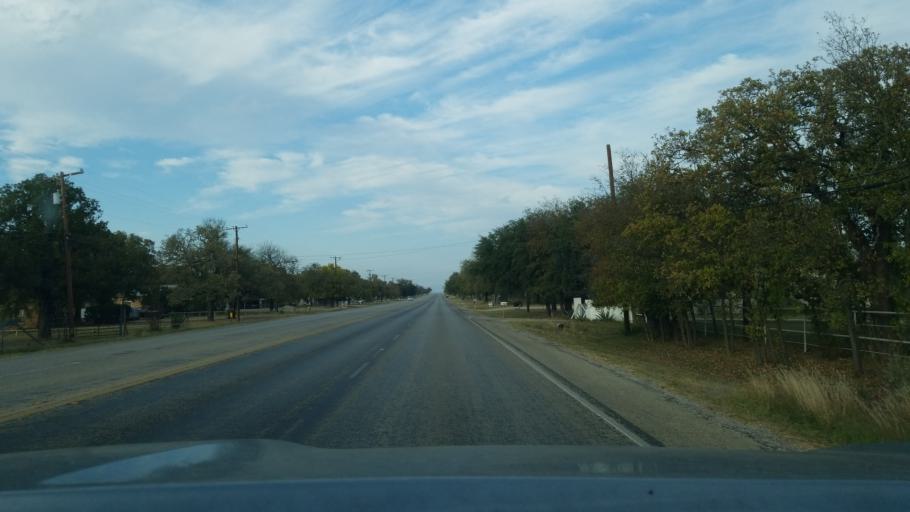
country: US
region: Texas
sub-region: Brown County
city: Early
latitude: 31.7604
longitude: -98.9578
